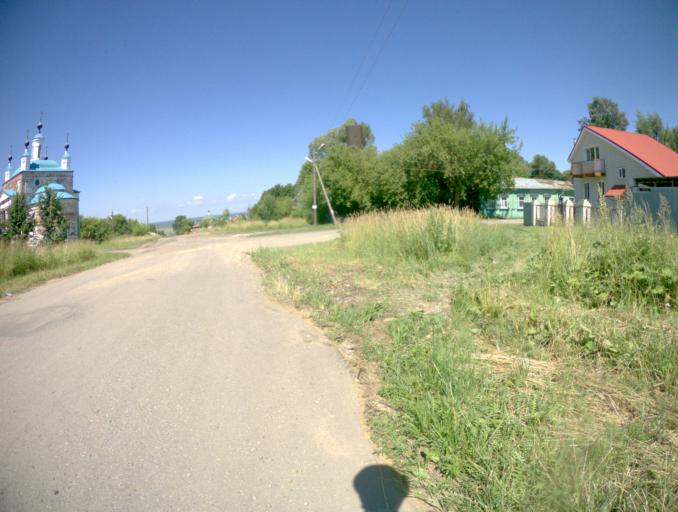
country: RU
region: Nizjnij Novgorod
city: Gorbatov
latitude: 56.1327
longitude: 43.0606
